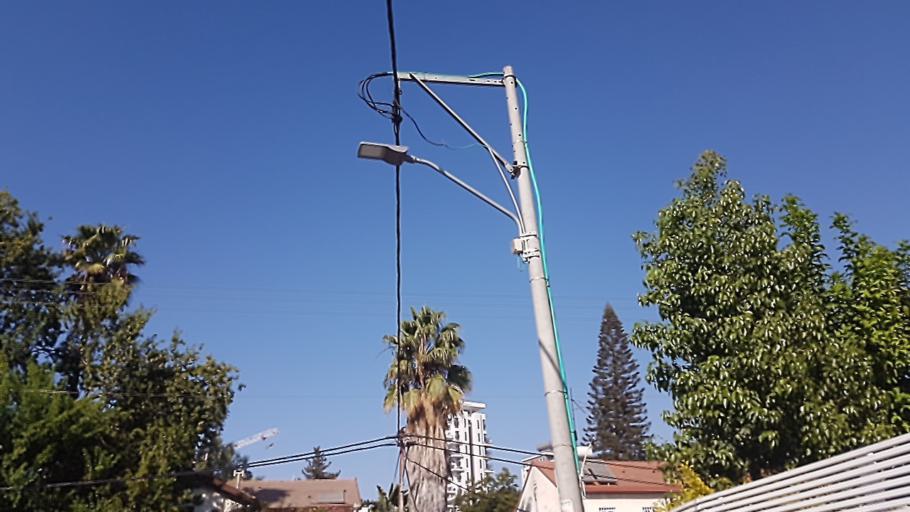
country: IL
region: Tel Aviv
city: Giv`atayim
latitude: 32.0575
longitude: 34.8281
